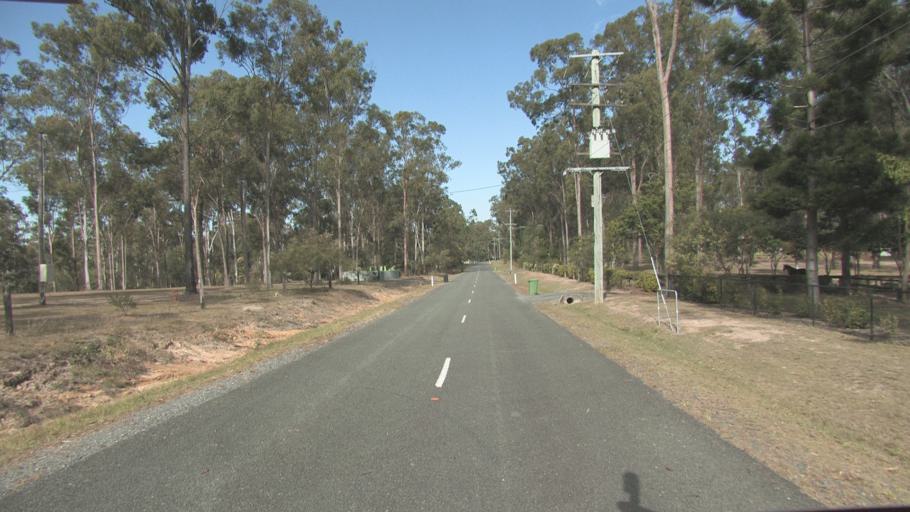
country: AU
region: Queensland
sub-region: Logan
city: North Maclean
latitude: -27.7445
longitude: 152.9734
